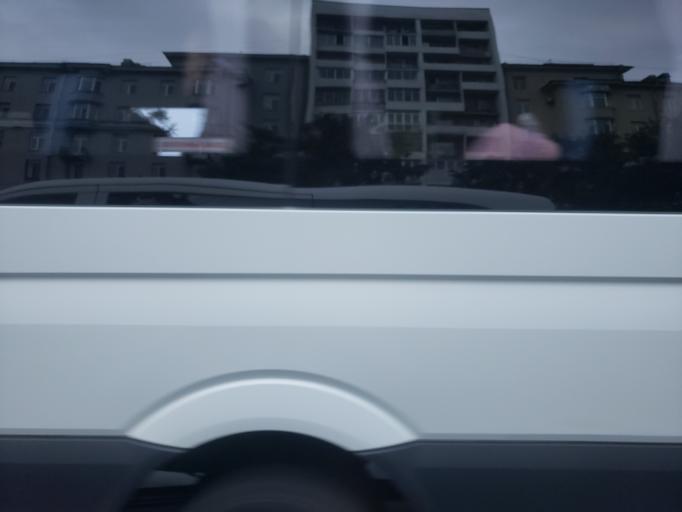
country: RU
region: St.-Petersburg
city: Vasyl'evsky Ostrov
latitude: 59.9321
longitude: 30.2360
